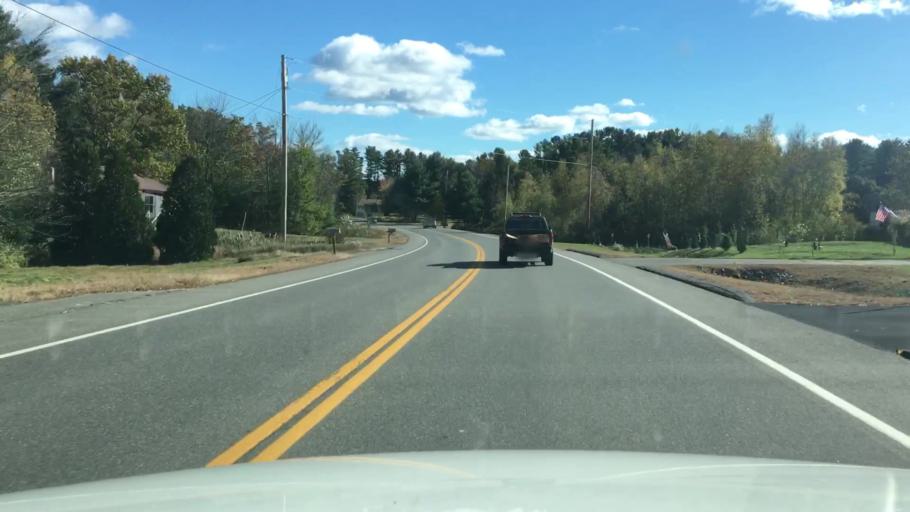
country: US
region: Maine
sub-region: York County
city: South Sanford
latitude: 43.3642
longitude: -70.6690
